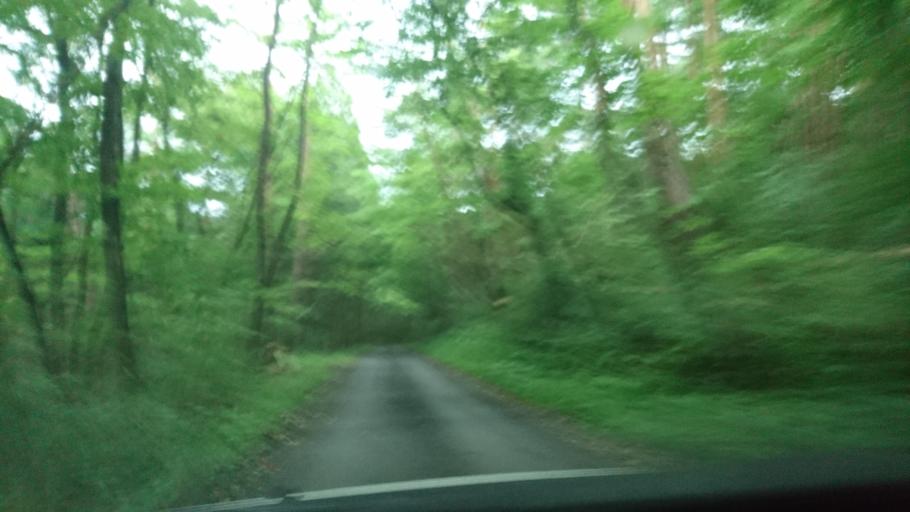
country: JP
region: Iwate
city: Ichinoseki
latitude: 38.9188
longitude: 141.1848
